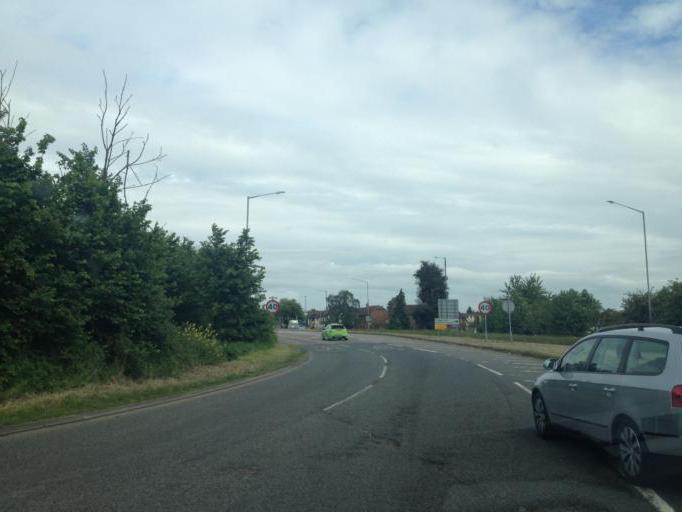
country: GB
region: England
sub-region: Buckinghamshire
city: Denham
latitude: 51.5627
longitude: -0.4976
